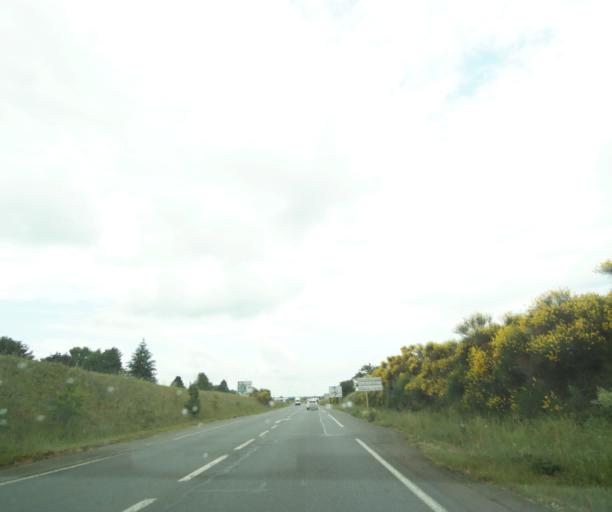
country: FR
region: Poitou-Charentes
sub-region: Departement des Deux-Sevres
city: Louzy
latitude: 46.9961
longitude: -0.1947
